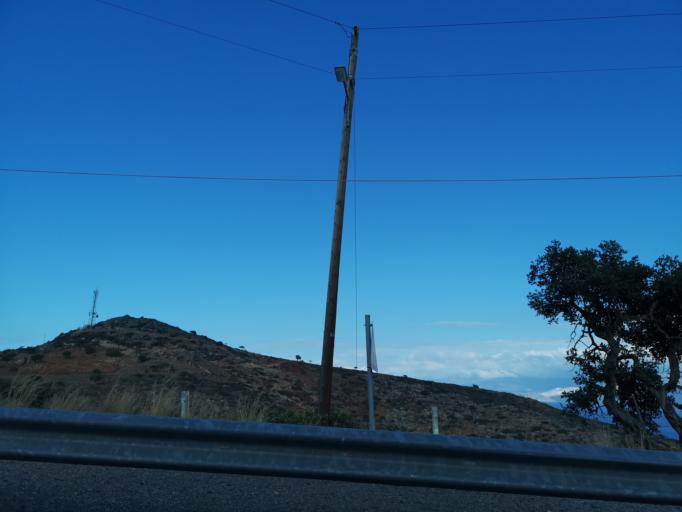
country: GR
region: Crete
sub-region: Nomos Lasithiou
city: Skhisma
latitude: 35.2296
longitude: 25.7237
